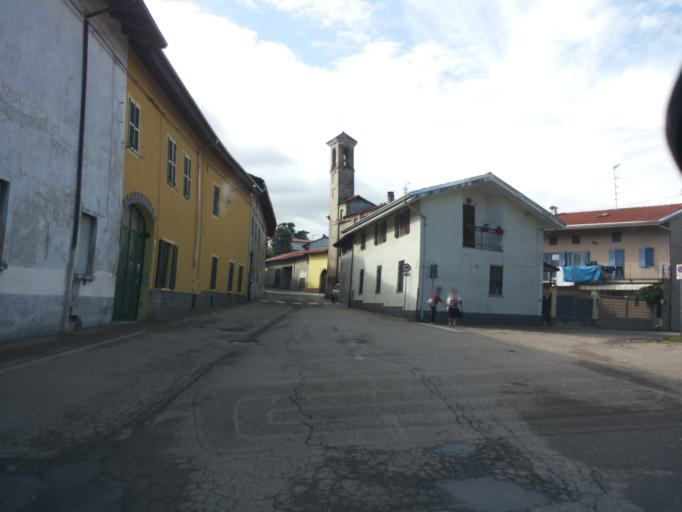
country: IT
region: Piedmont
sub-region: Provincia di Vercelli
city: Moncrivello
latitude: 45.3295
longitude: 8.0009
